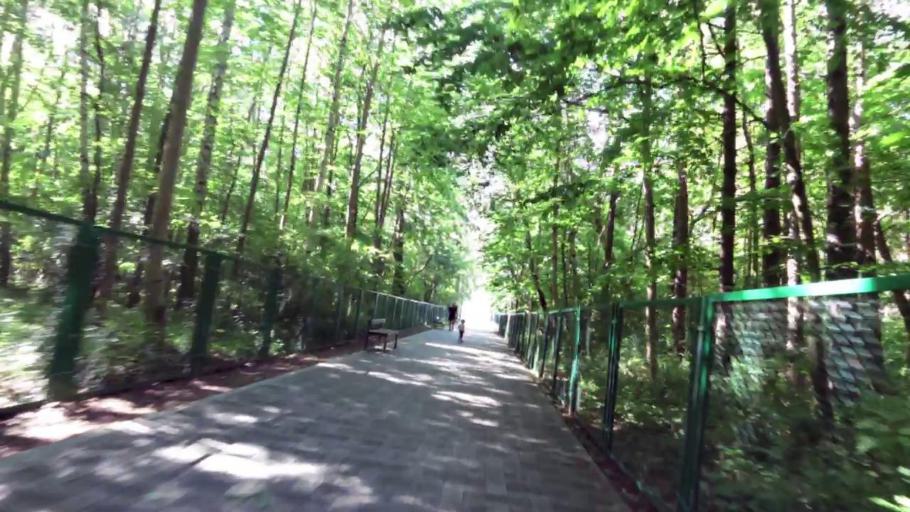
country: PL
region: West Pomeranian Voivodeship
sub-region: Powiat koszalinski
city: Mielno
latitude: 54.2647
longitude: 16.0678
